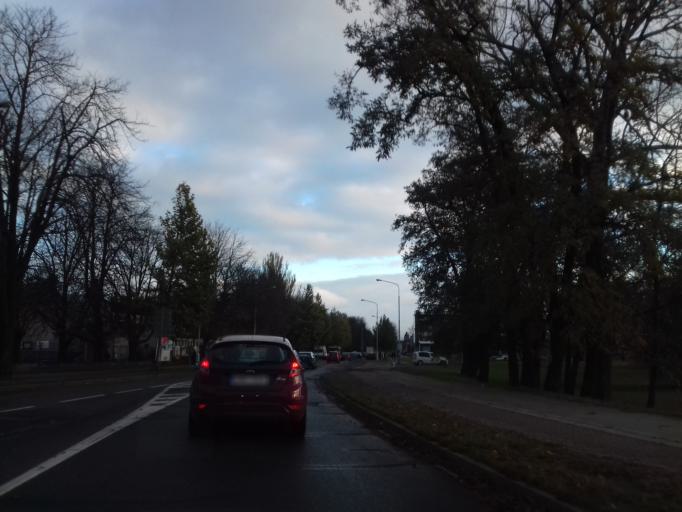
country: CZ
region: Olomoucky
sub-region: Okres Olomouc
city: Olomouc
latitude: 49.5899
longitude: 17.2607
